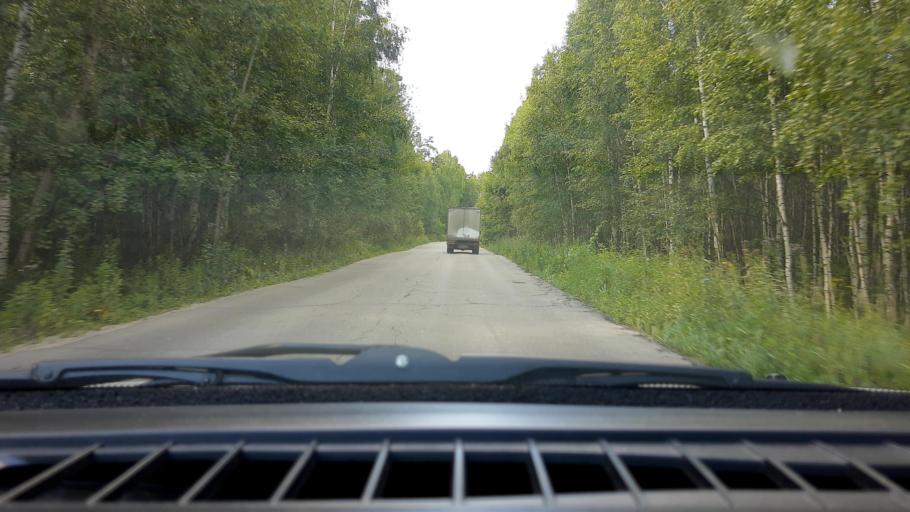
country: RU
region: Nizjnij Novgorod
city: Babino
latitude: 56.3148
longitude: 43.6253
